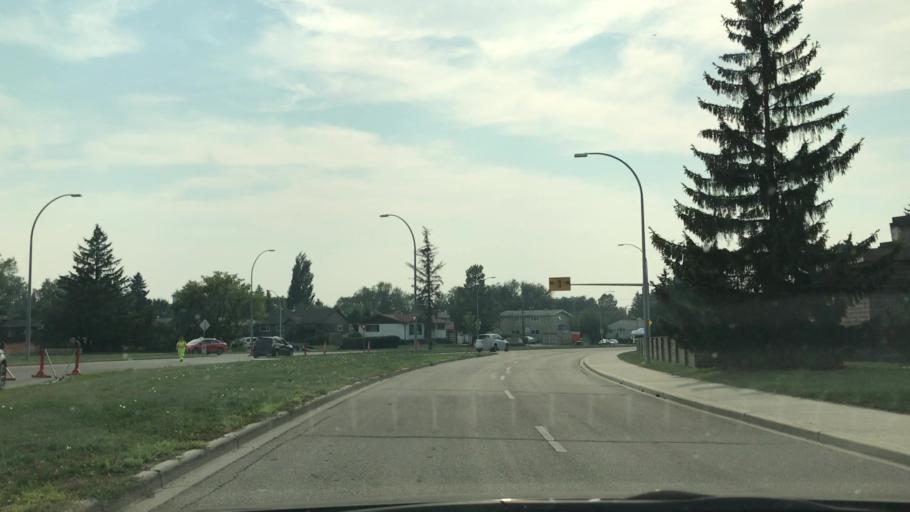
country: CA
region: Alberta
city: Edmonton
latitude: 53.4985
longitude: -113.5015
